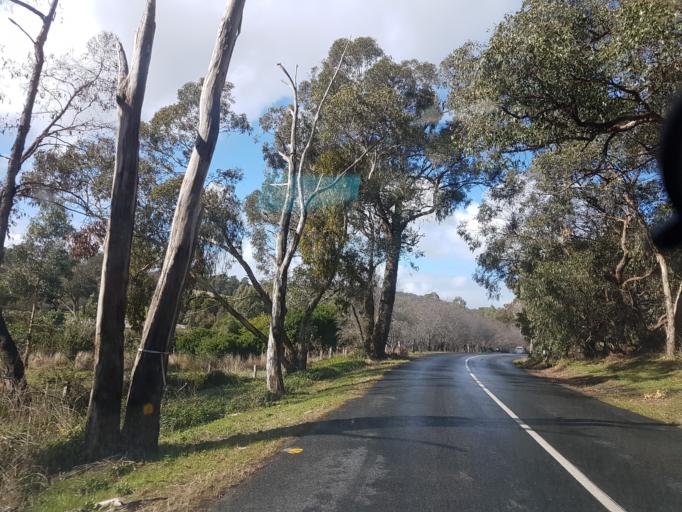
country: AU
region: South Australia
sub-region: Adelaide Hills
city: Heathfield
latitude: -35.0407
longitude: 138.7078
